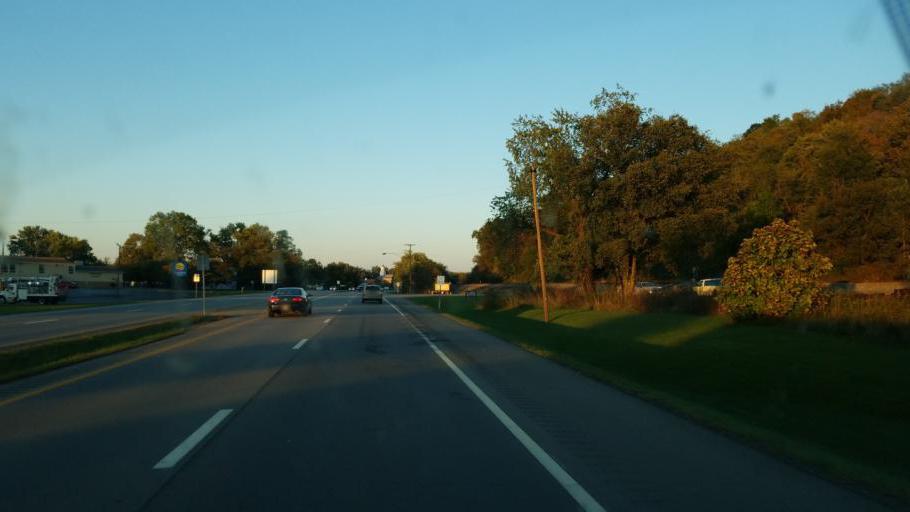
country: US
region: Ohio
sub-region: Pike County
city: Piketon
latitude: 39.0640
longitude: -83.0149
